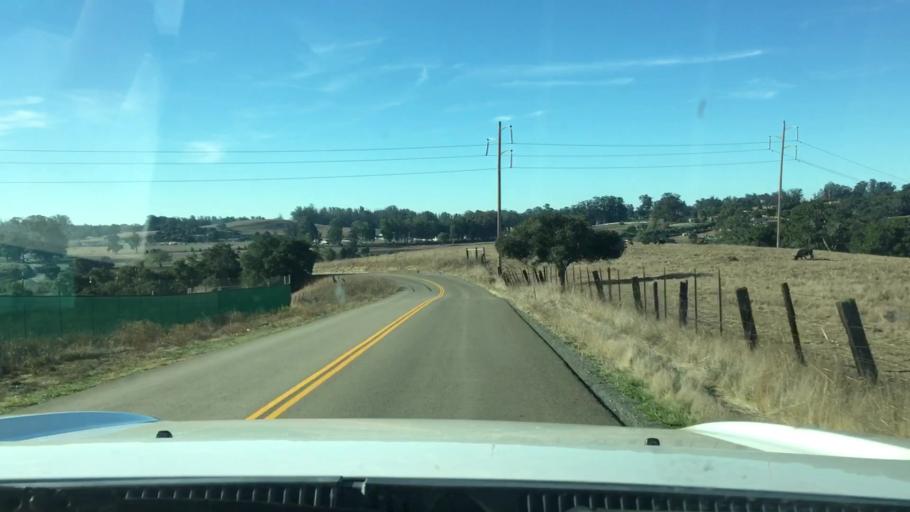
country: US
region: California
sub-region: San Luis Obispo County
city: Arroyo Grande
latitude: 35.0991
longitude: -120.5600
